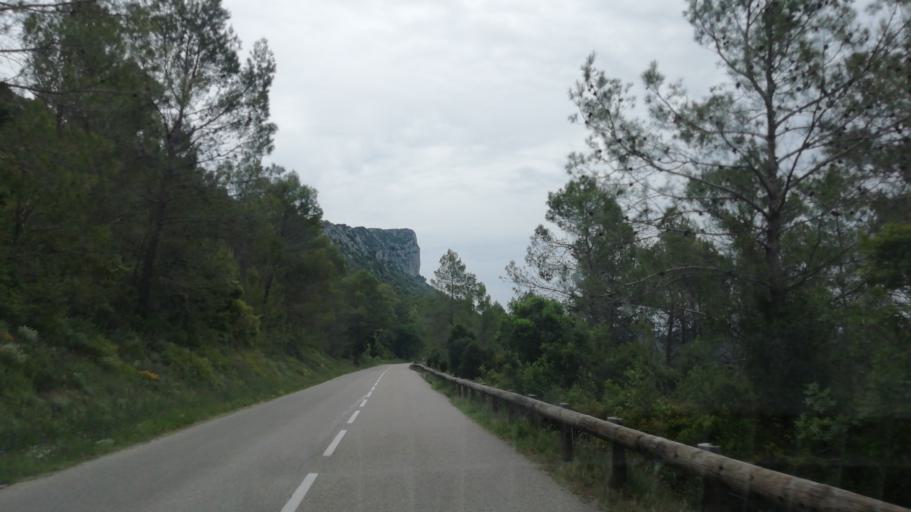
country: FR
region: Languedoc-Roussillon
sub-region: Departement de l'Herault
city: Saint-Mathieu-de-Treviers
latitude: 43.7908
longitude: 3.8114
